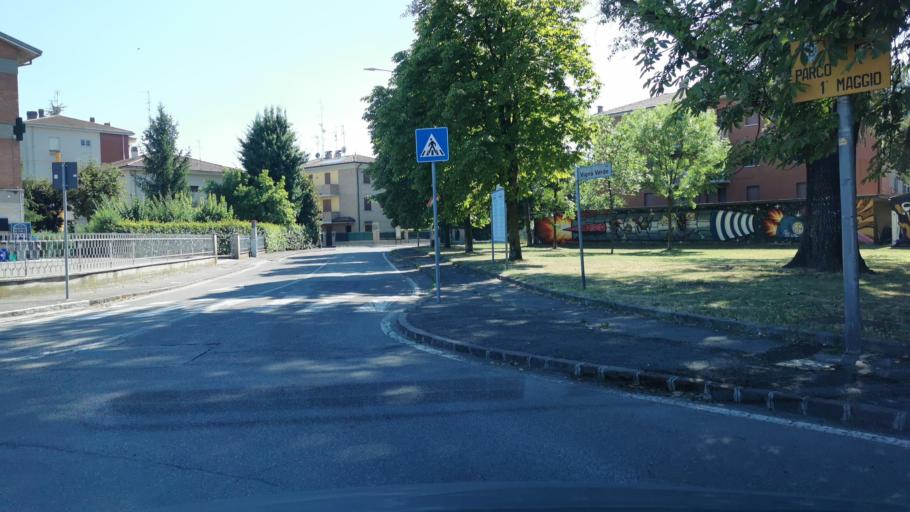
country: IT
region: Emilia-Romagna
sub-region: Provincia di Modena
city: Villanova
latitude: 44.6861
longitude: 10.8939
